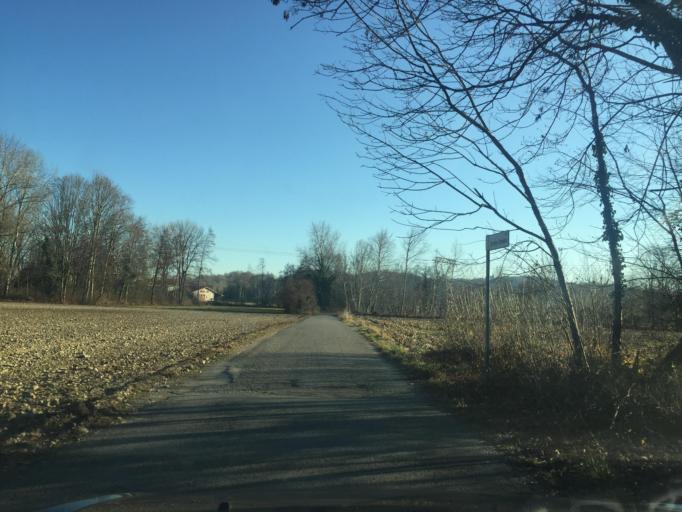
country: IT
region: Friuli Venezia Giulia
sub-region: Provincia di Udine
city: Buia
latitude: 46.2408
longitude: 13.1122
